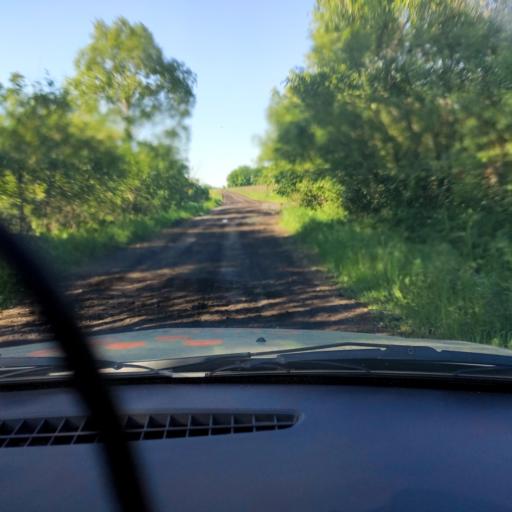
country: RU
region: Bashkortostan
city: Avdon
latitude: 54.5614
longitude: 55.8272
